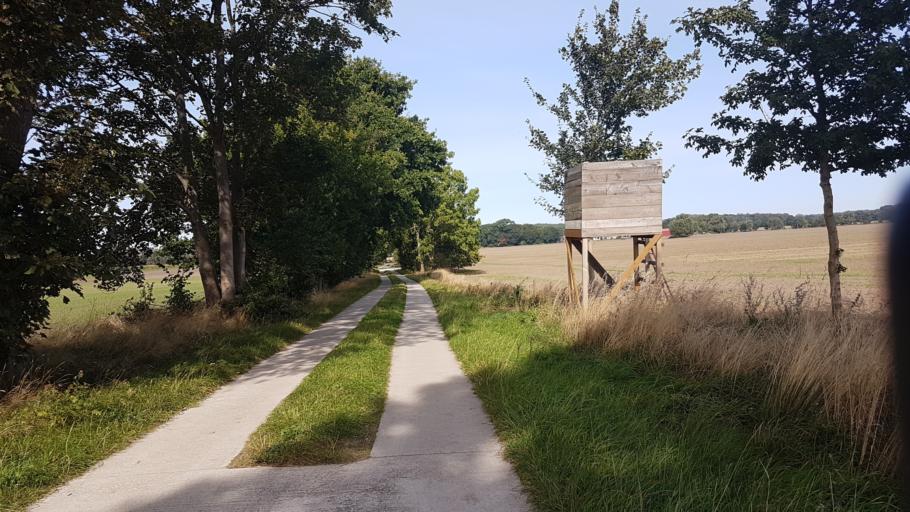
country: DE
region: Mecklenburg-Vorpommern
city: Samtens
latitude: 54.3973
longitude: 13.2596
